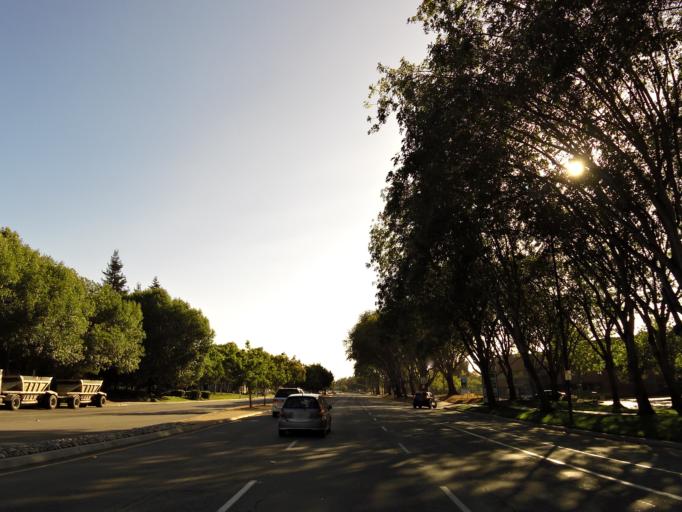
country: US
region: California
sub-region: Santa Clara County
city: Santa Clara
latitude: 37.3857
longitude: -121.9286
